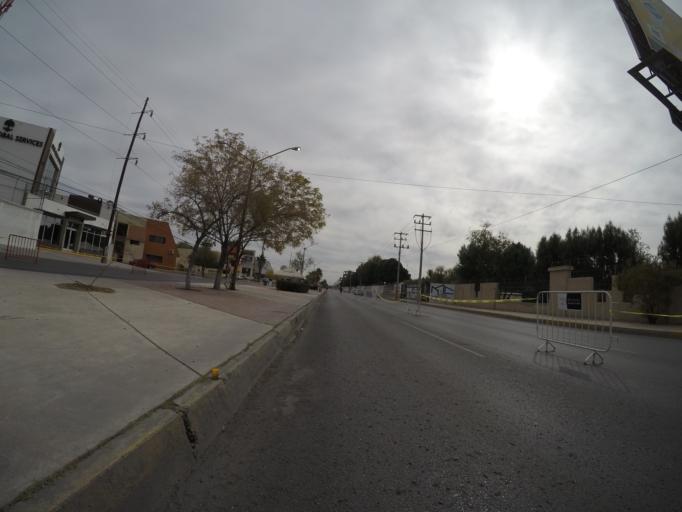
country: MX
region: Chihuahua
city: Ciudad Juarez
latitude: 31.7284
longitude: -106.4072
